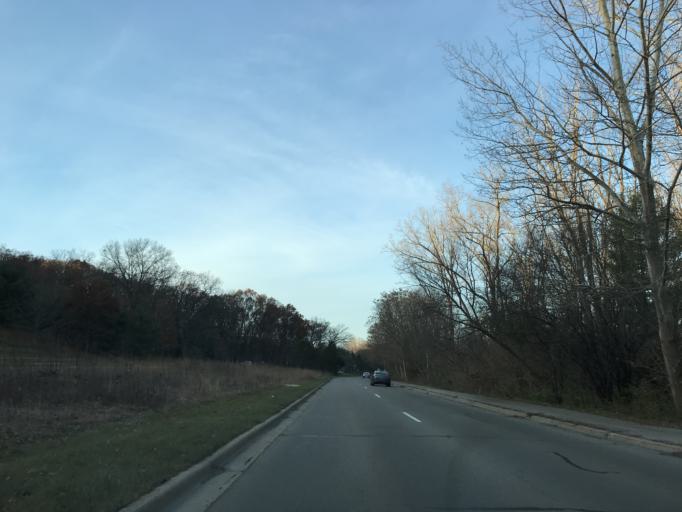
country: US
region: Michigan
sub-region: Washtenaw County
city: Ann Arbor
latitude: 42.2852
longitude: -83.7021
